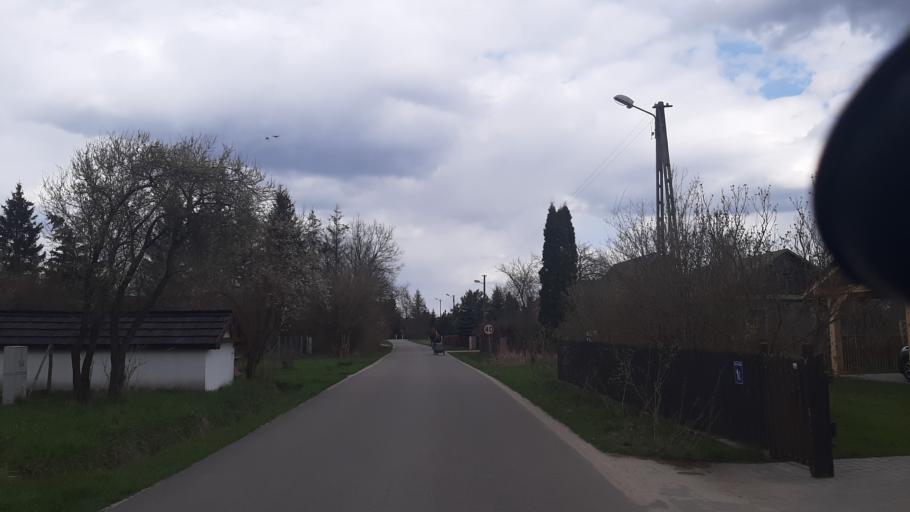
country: PL
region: Lublin Voivodeship
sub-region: Powiat lubelski
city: Niemce
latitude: 51.3816
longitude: 22.5561
